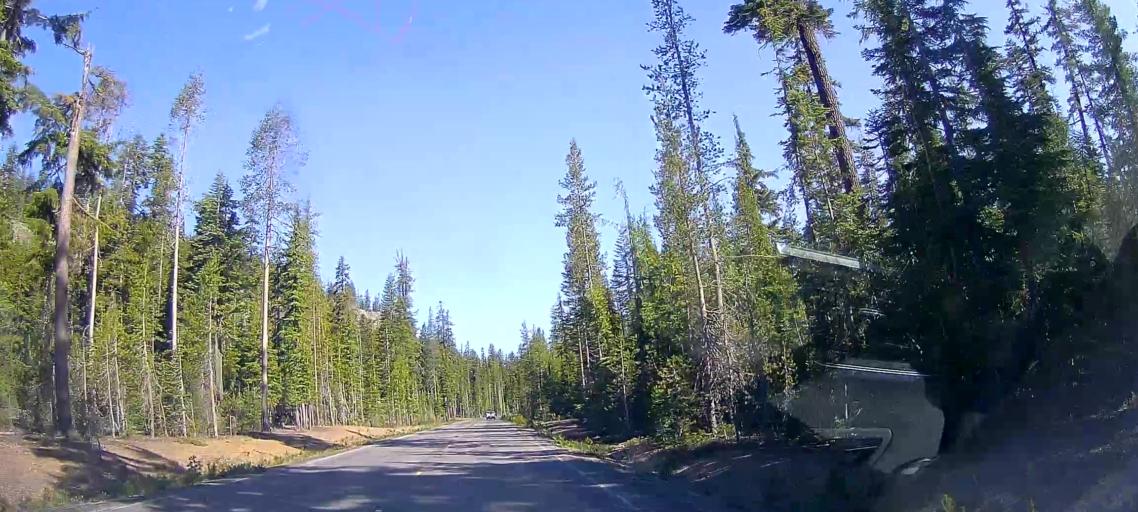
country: US
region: Oregon
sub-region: Jackson County
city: Shady Cove
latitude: 42.8518
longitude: -122.1505
